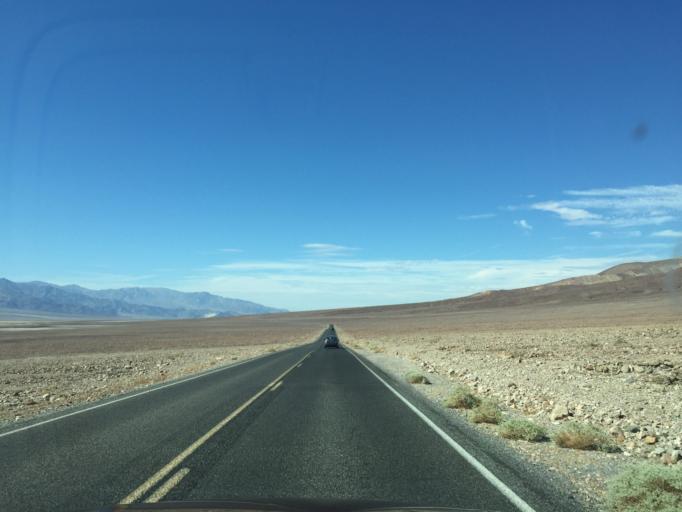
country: US
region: Nevada
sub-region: Nye County
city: Beatty
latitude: 36.2598
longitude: -116.7789
